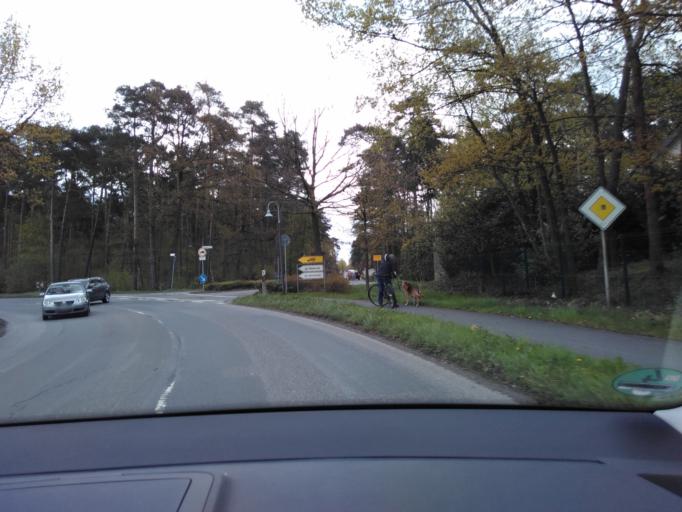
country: DE
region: North Rhine-Westphalia
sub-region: Regierungsbezirk Detmold
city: Verl
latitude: 51.8858
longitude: 8.4582
